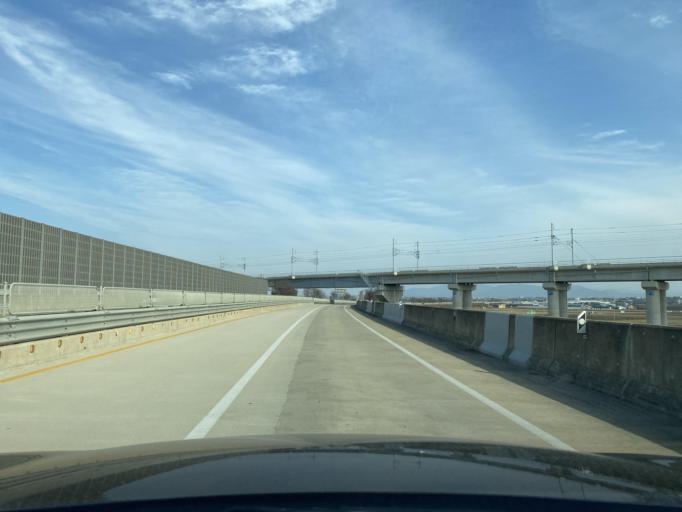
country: KR
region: Chungcheongnam-do
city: Hongsung
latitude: 36.6912
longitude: 126.7226
